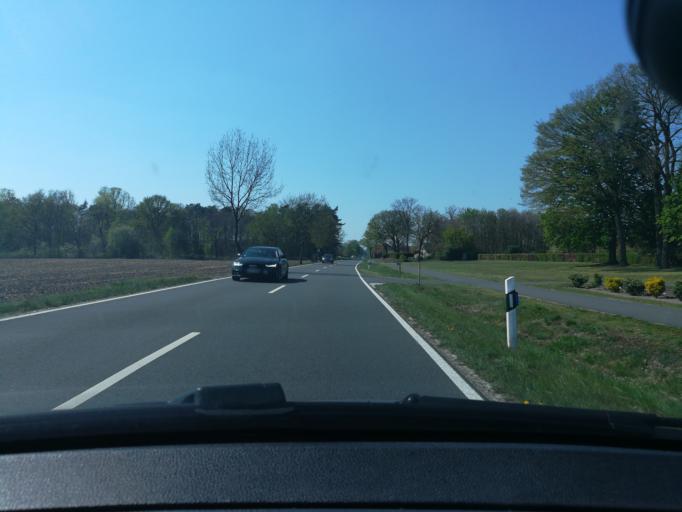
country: DE
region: North Rhine-Westphalia
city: Versmold
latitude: 52.0058
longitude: 8.1916
